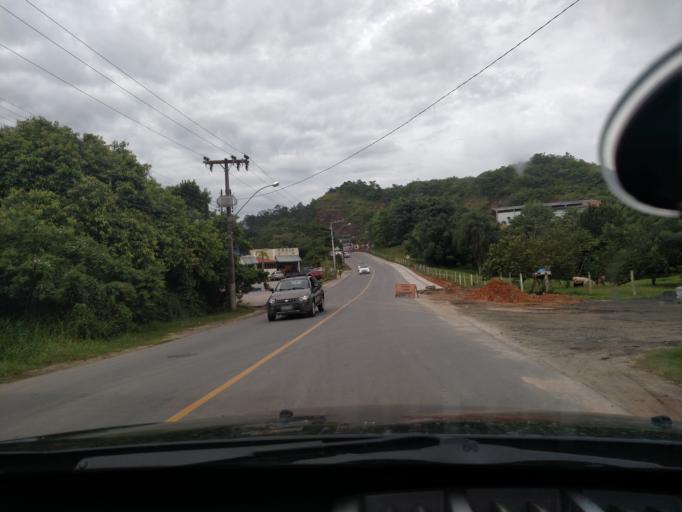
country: BR
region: Santa Catarina
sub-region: Porto Belo
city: Porto Belo
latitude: -27.1547
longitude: -48.5127
